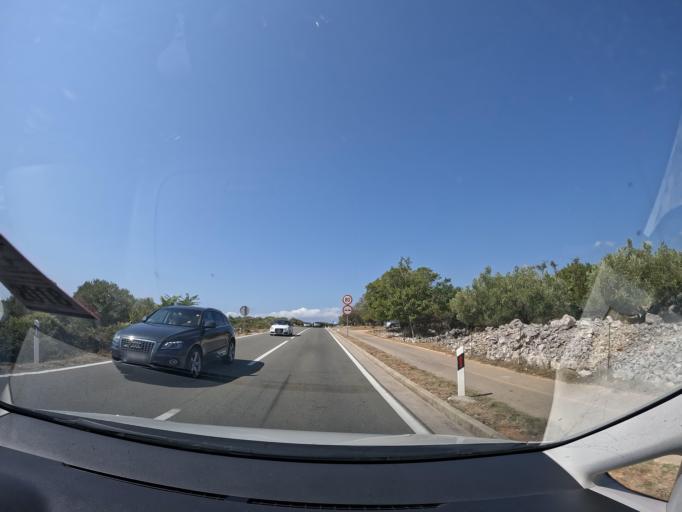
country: HR
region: Primorsko-Goranska
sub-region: Grad Krk
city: Krk
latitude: 45.0315
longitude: 14.6014
